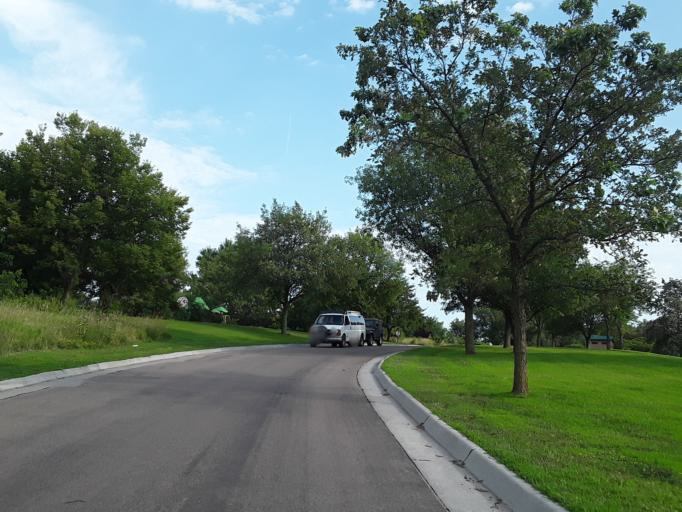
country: US
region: Nebraska
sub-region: Saunders County
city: Ashland
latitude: 41.0200
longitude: -96.3121
